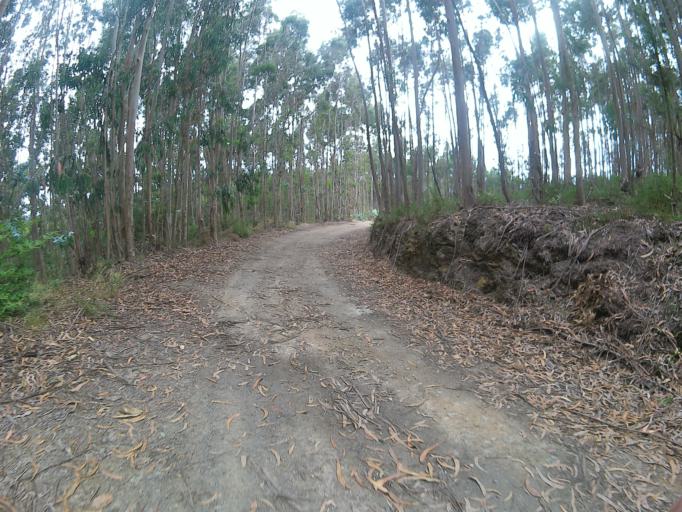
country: PT
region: Aveiro
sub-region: Albergaria-A-Velha
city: Branca
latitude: 40.7610
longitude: -8.4325
